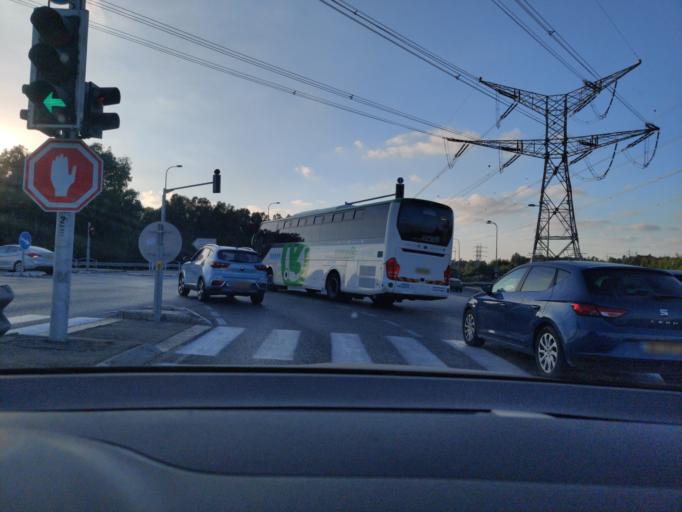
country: IL
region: Haifa
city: Hadera
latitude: 32.4477
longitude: 34.9435
